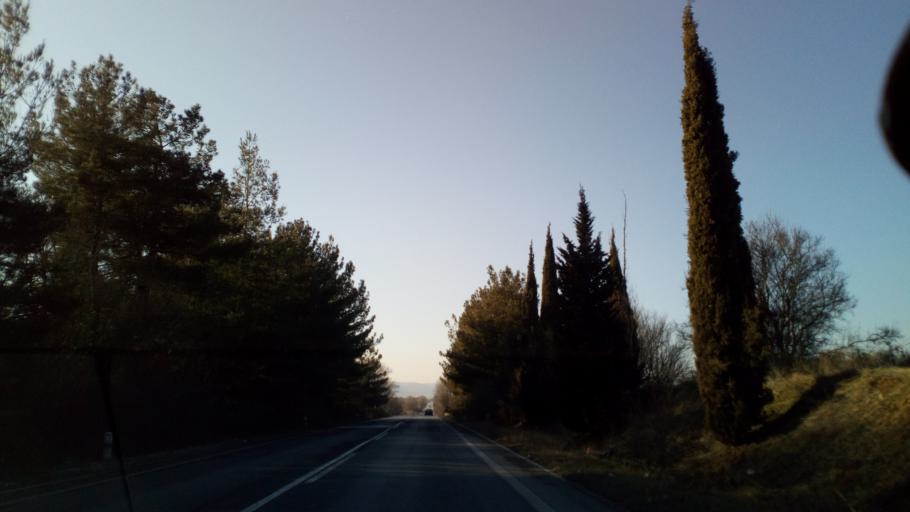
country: GR
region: Central Macedonia
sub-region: Nomos Thessalonikis
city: Agios Vasileios
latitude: 40.6571
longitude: 23.1320
